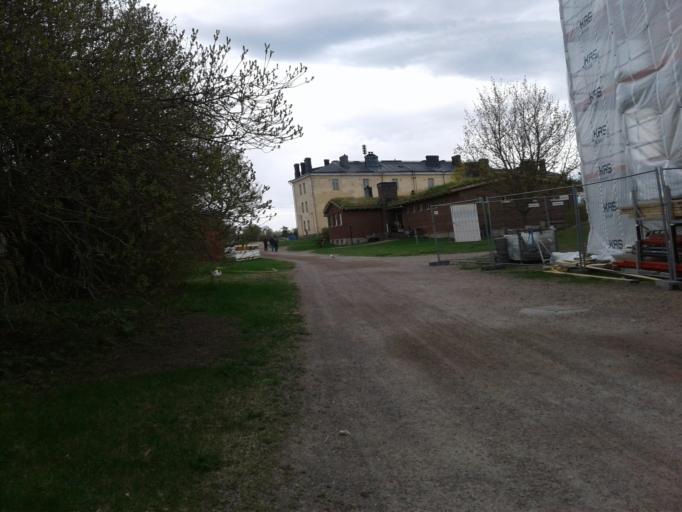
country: FI
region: Uusimaa
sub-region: Helsinki
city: Helsinki
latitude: 60.1486
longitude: 24.9755
